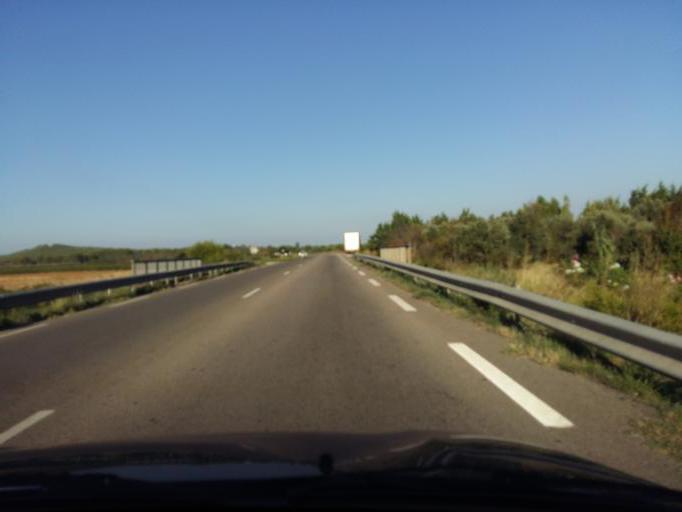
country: FR
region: Languedoc-Roussillon
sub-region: Departement du Gard
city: Saint-Gervasy
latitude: 43.8700
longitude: 4.4555
